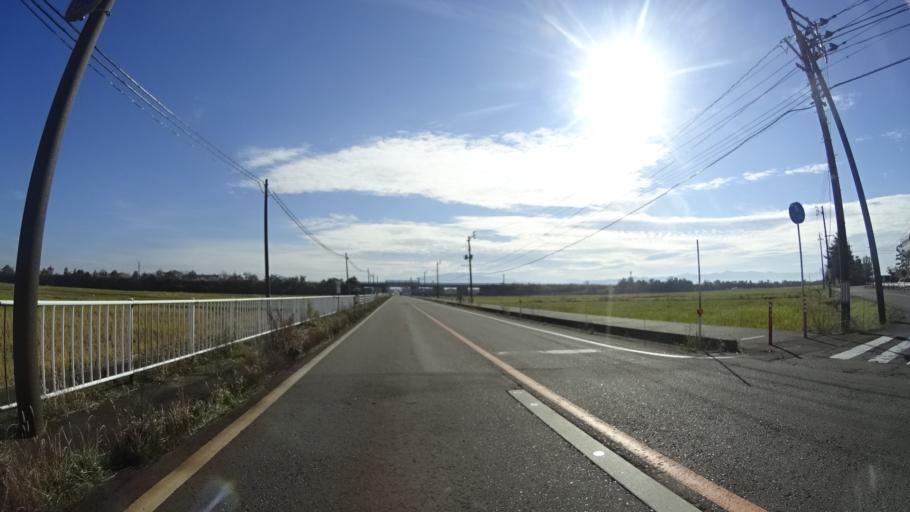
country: JP
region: Niigata
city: Mitsuke
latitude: 37.5505
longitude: 138.8698
